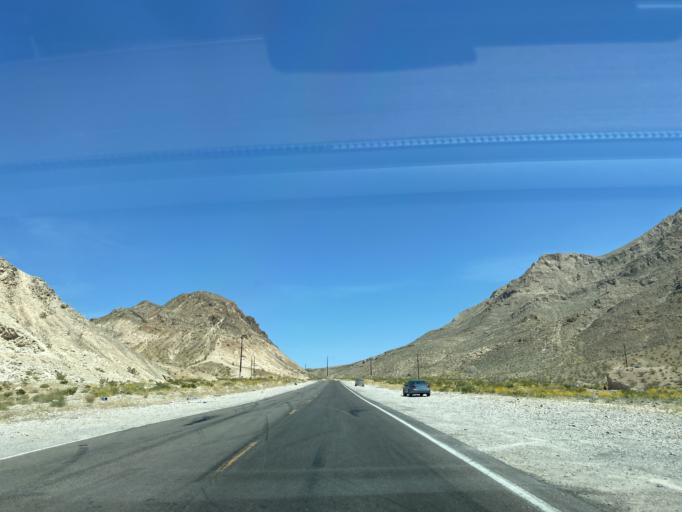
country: US
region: Nevada
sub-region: Clark County
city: Sunrise Manor
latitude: 36.1989
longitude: -115.0081
